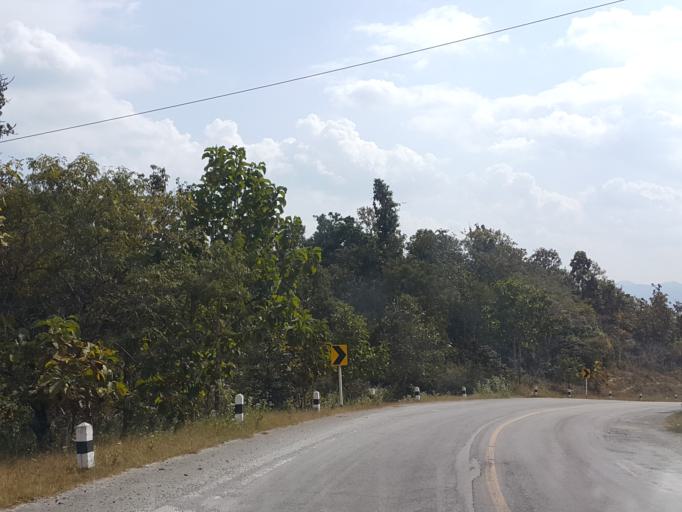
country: TH
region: Chiang Mai
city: Om Koi
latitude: 17.8171
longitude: 98.3680
